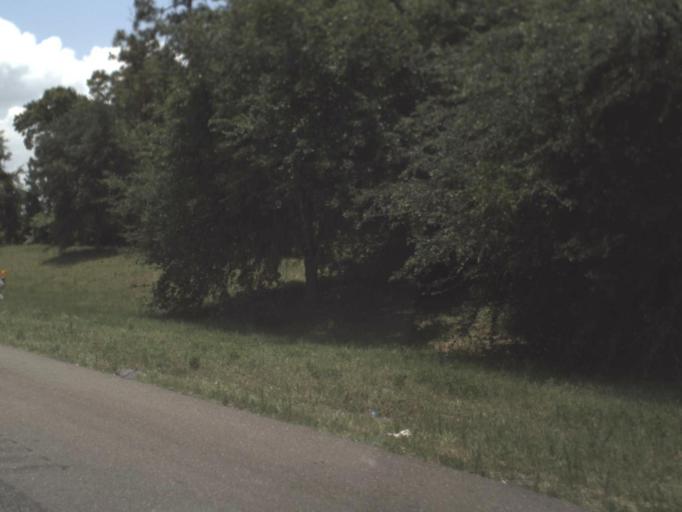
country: US
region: Florida
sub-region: Duval County
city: Jacksonville
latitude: 30.4278
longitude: -81.5737
